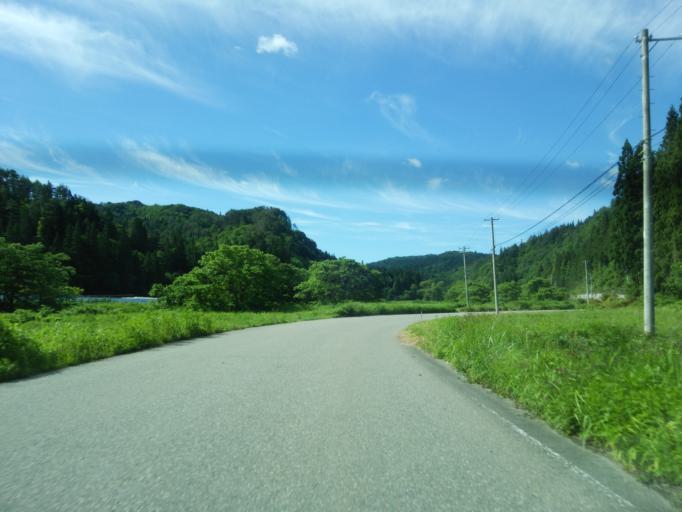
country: JP
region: Fukushima
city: Kitakata
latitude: 37.4218
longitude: 139.8102
